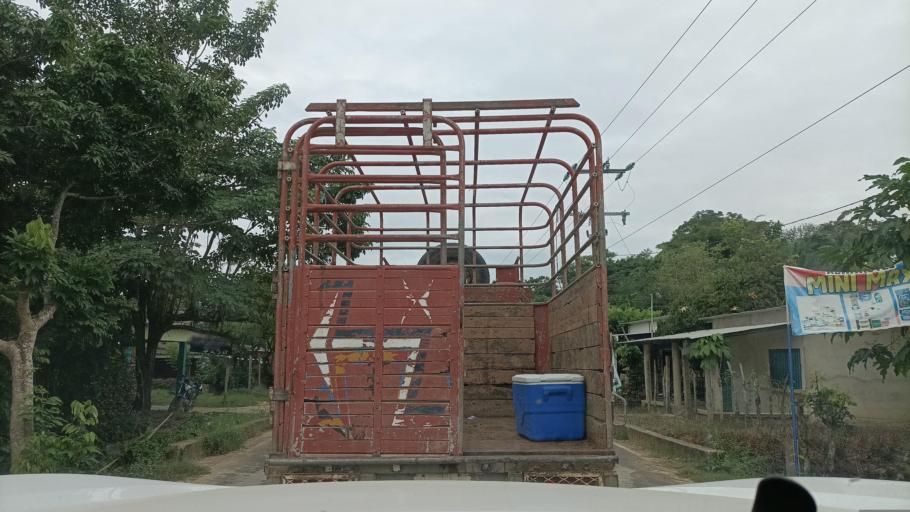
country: MX
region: Veracruz
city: Hidalgotitlan
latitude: 17.6580
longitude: -94.4055
